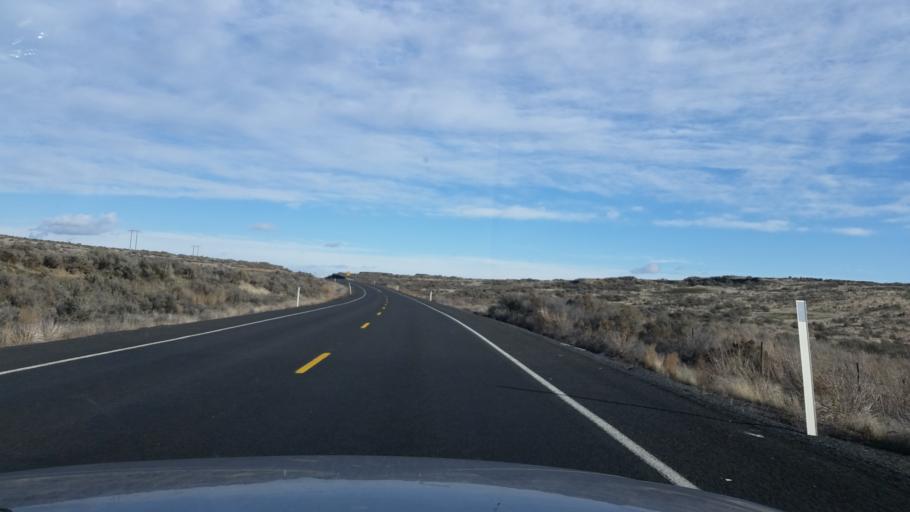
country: US
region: Washington
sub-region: Adams County
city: Ritzville
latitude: 47.3408
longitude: -118.6142
